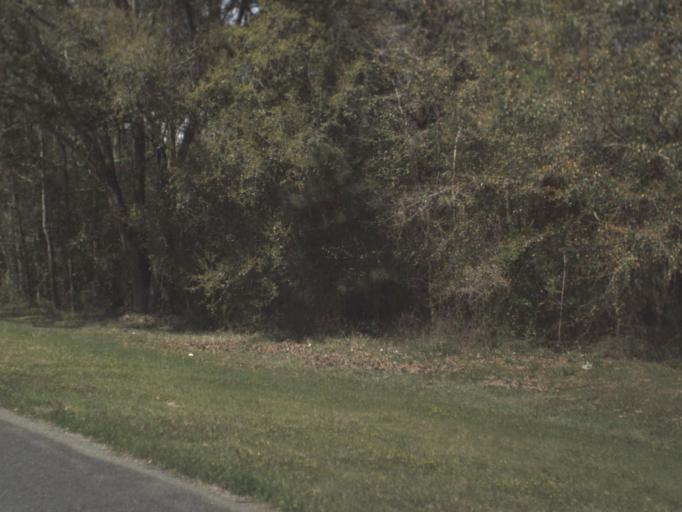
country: US
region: Florida
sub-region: Holmes County
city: Bonifay
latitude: 30.7628
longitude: -85.8597
